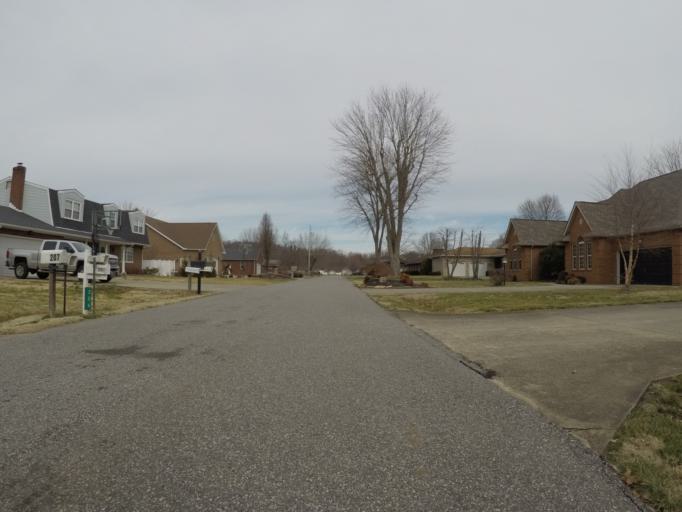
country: US
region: West Virginia
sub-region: Cabell County
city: Pea Ridge
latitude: 38.4489
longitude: -82.3515
